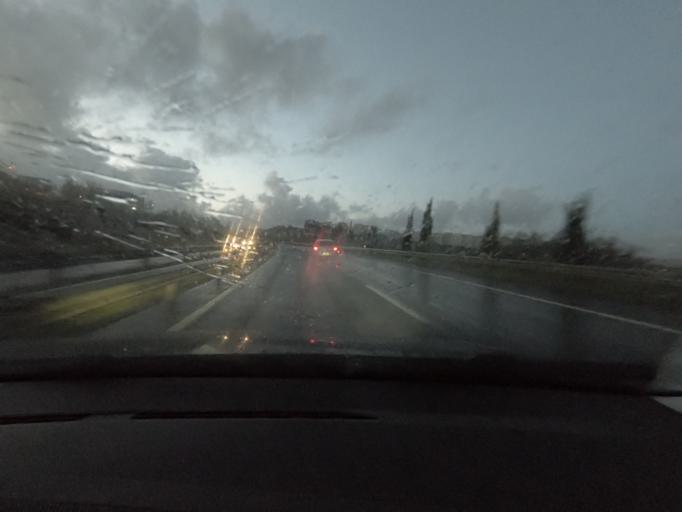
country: PT
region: Lisbon
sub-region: Oeiras
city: Barcarena
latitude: 38.7400
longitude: -9.2993
